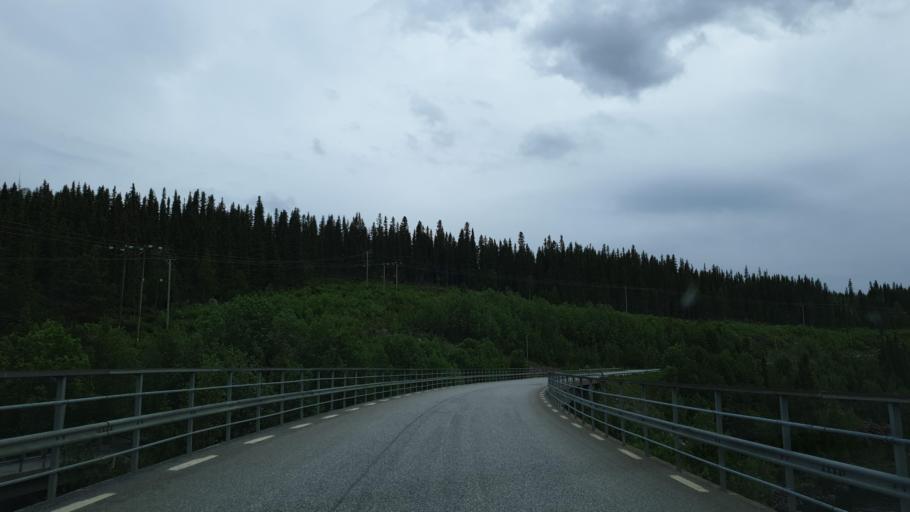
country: SE
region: Vaesterbotten
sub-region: Storumans Kommun
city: Fristad
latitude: 65.4242
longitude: 16.1716
